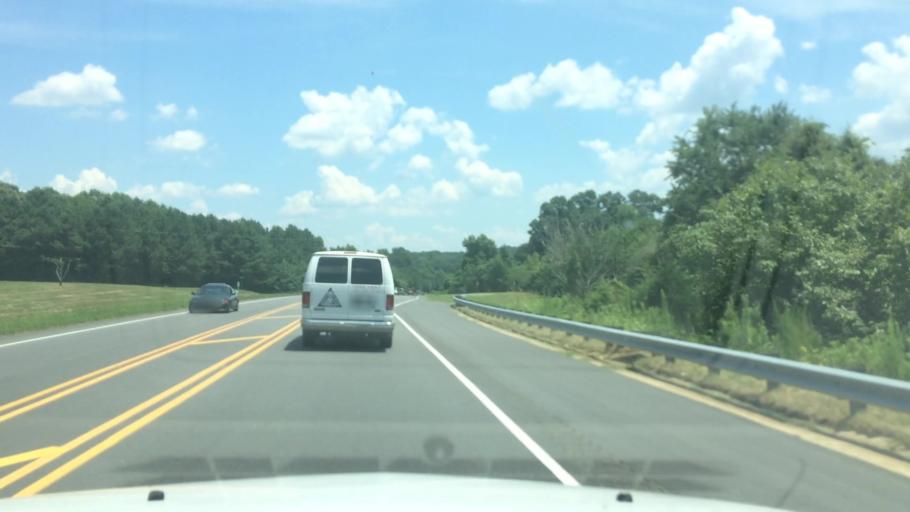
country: US
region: North Carolina
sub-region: Alexander County
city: Stony Point
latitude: 35.8151
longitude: -80.9853
